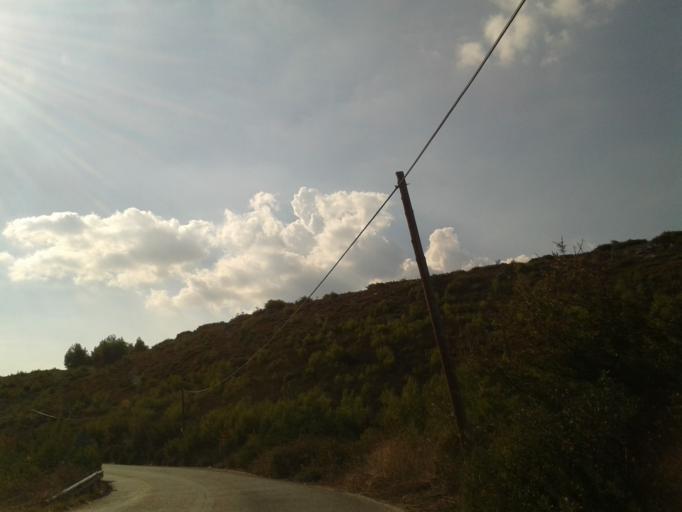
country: GR
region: Attica
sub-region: Nomarchia Anatolikis Attikis
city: Stamata
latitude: 38.1531
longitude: 23.8957
